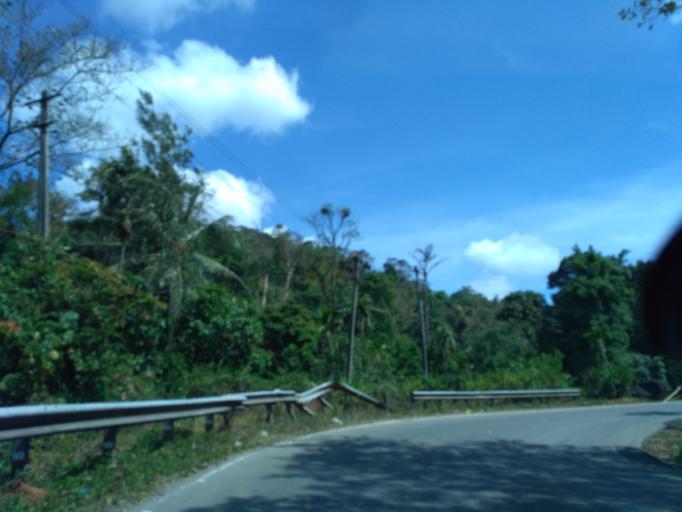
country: IN
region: Karnataka
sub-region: Kodagu
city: Madikeri
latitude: 12.4375
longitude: 75.6571
